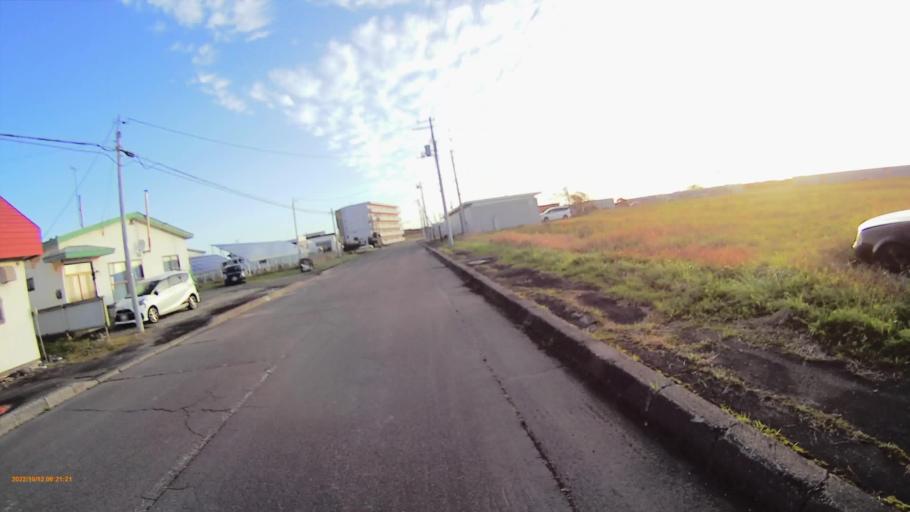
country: JP
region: Hokkaido
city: Kushiro
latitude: 42.8869
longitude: 143.9333
